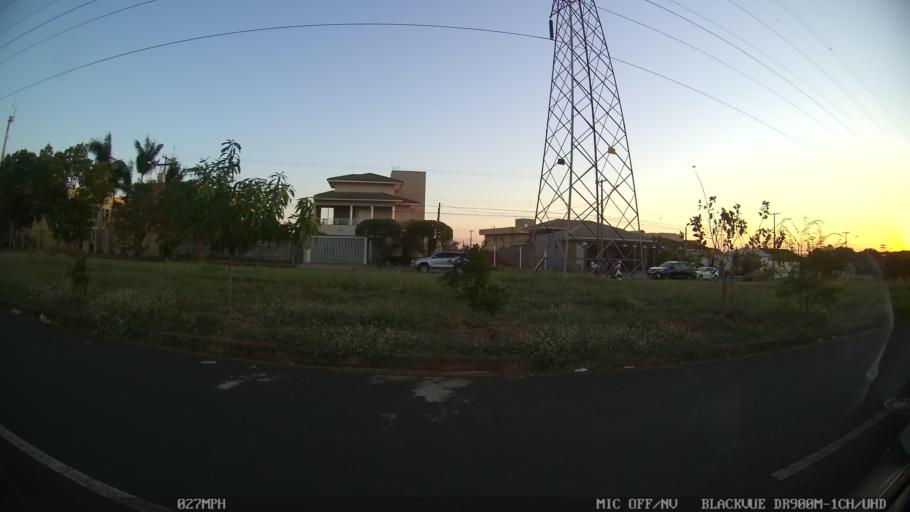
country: BR
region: Sao Paulo
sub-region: Sao Jose Do Rio Preto
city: Sao Jose do Rio Preto
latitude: -20.7983
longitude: -49.3490
